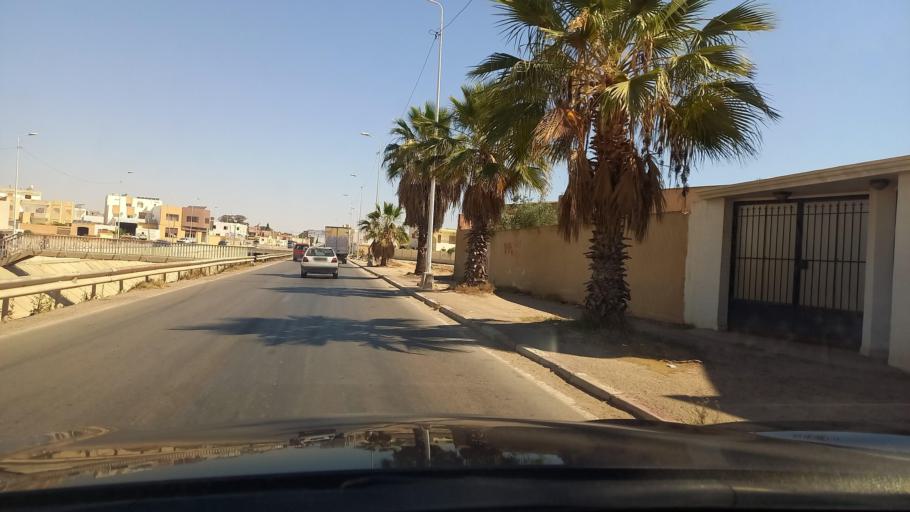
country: TN
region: Safaqis
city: Sfax
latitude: 34.7279
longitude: 10.7261
